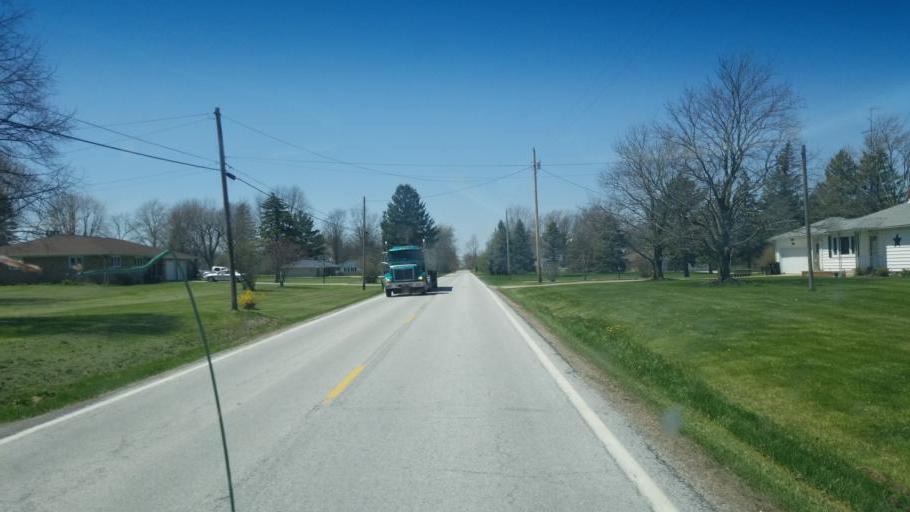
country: US
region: Ohio
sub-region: Huron County
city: New London
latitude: 41.0839
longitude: -82.3801
